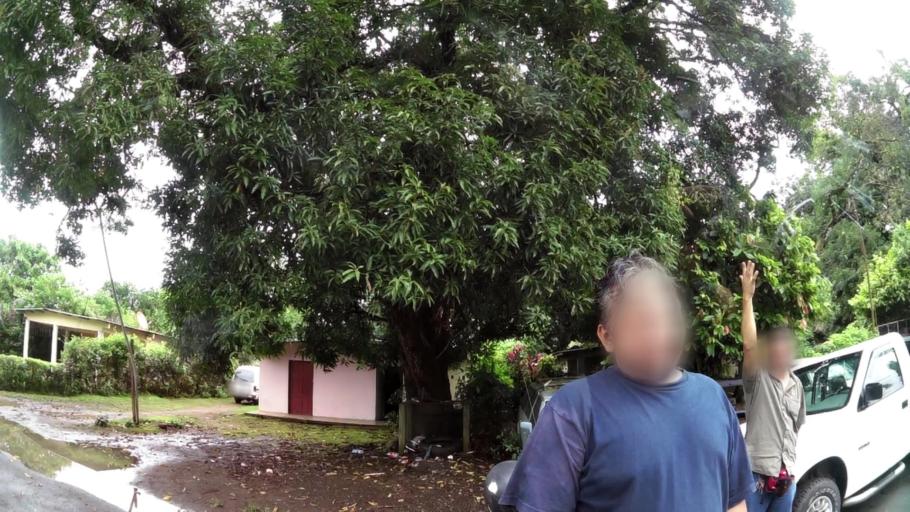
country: PA
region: Chiriqui
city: David
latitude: 8.4254
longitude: -82.4478
